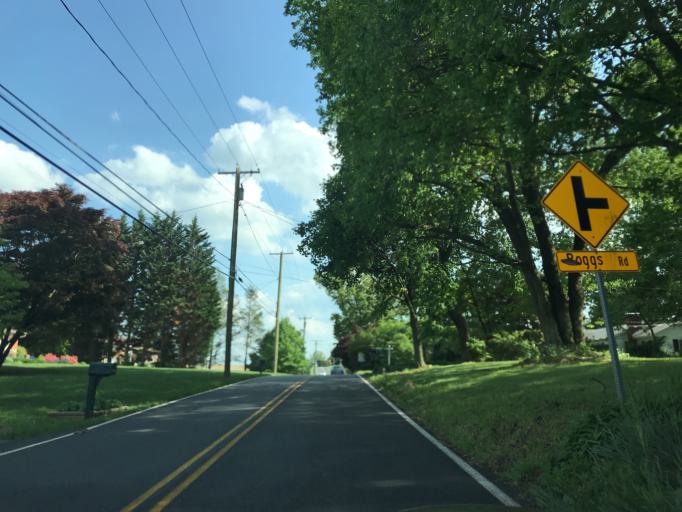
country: US
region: Maryland
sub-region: Harford County
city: Bel Air North
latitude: 39.5583
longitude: -76.3983
